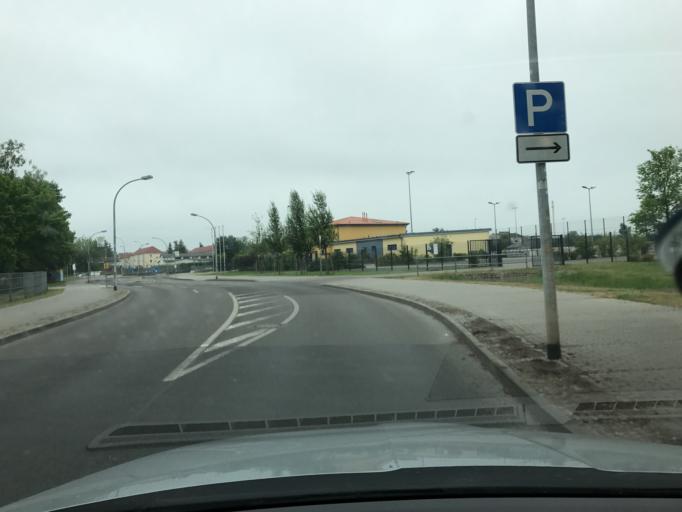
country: DE
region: Brandenburg
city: Falkensee
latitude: 52.5644
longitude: 13.0793
